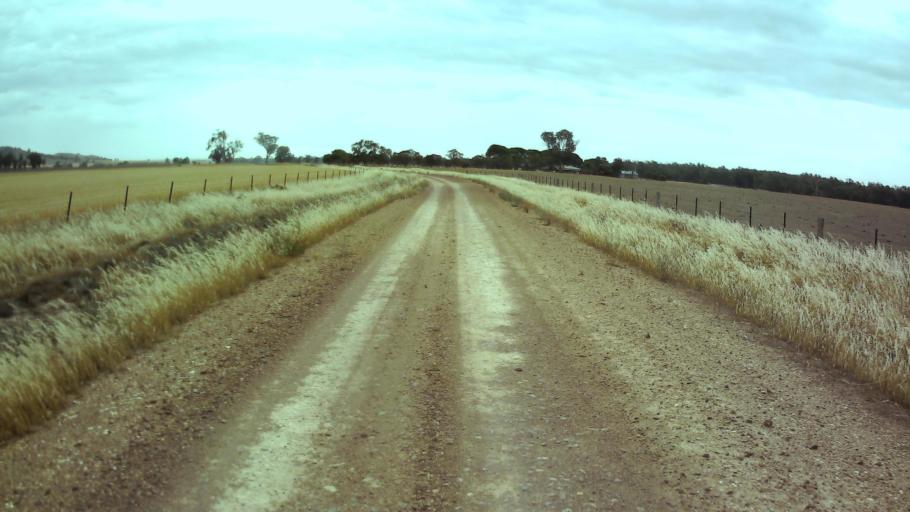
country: AU
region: New South Wales
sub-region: Weddin
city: Grenfell
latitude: -33.9194
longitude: 148.2859
